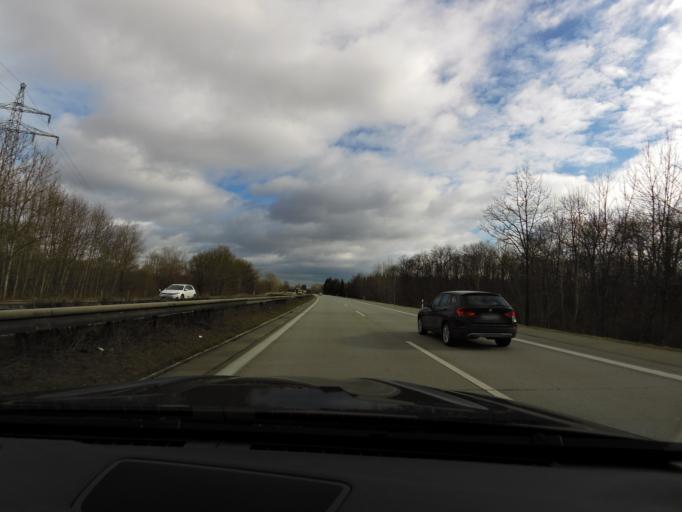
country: DE
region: Bavaria
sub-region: Lower Bavaria
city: Eching
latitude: 48.5102
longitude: 12.0424
